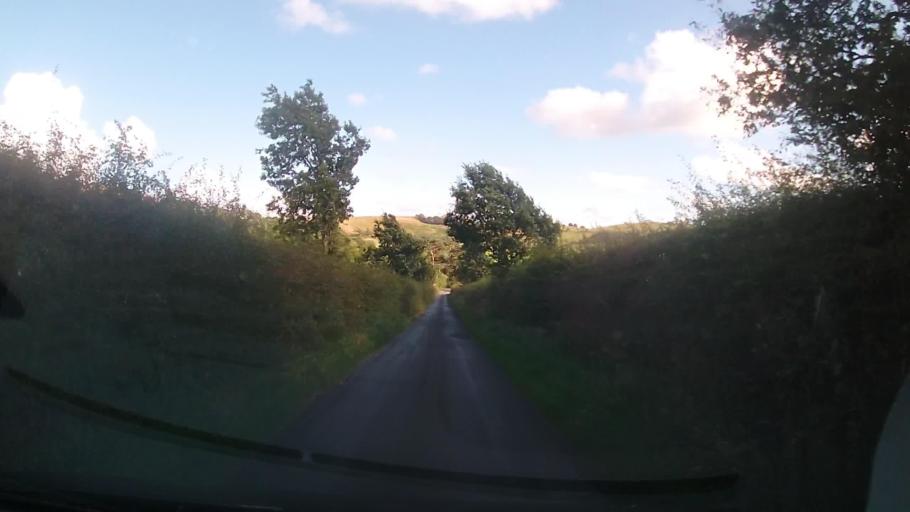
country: GB
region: England
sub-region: Shropshire
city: Norbury
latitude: 52.5641
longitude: -2.8990
